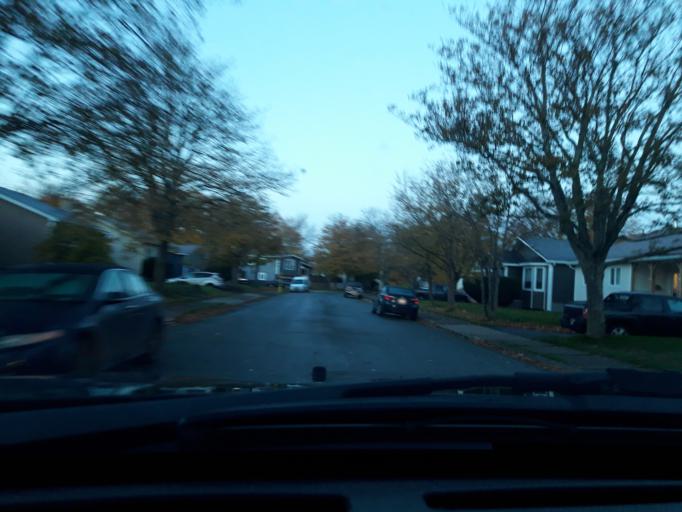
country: CA
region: Newfoundland and Labrador
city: St. John's
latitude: 47.5632
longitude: -52.7463
